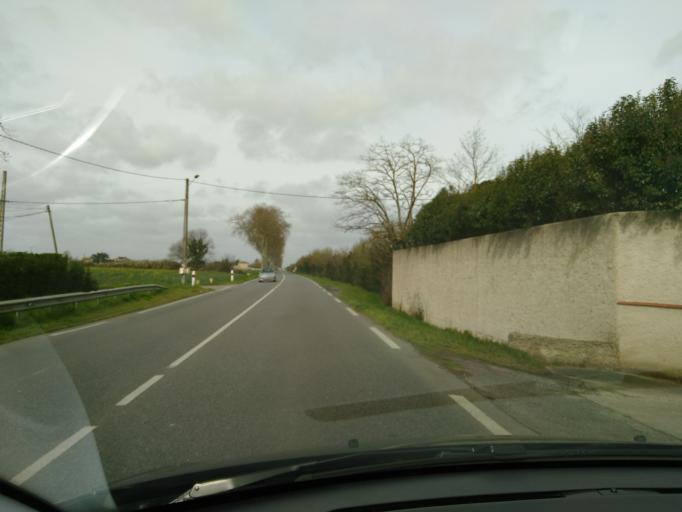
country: FR
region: Midi-Pyrenees
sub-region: Departement de la Haute-Garonne
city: Seilh
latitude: 43.7068
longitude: 1.3425
